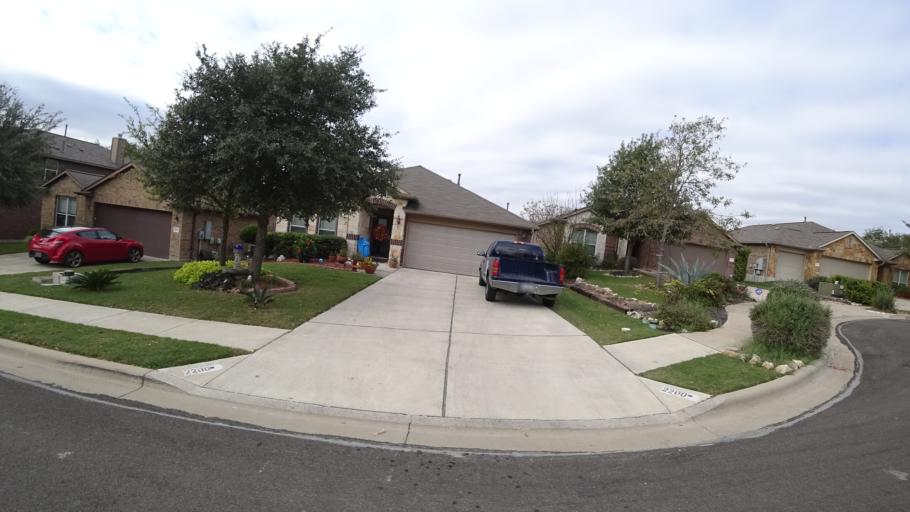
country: US
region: Texas
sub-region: Travis County
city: Manchaca
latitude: 30.1453
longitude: -97.8447
